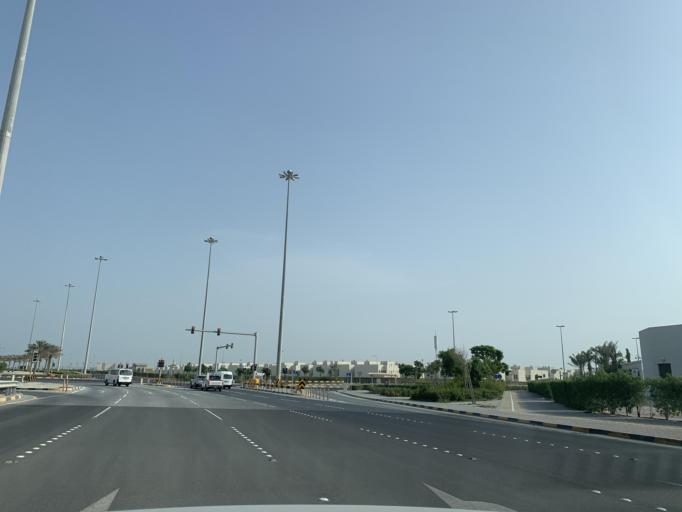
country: BH
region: Muharraq
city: Al Muharraq
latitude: 26.3059
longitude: 50.6396
